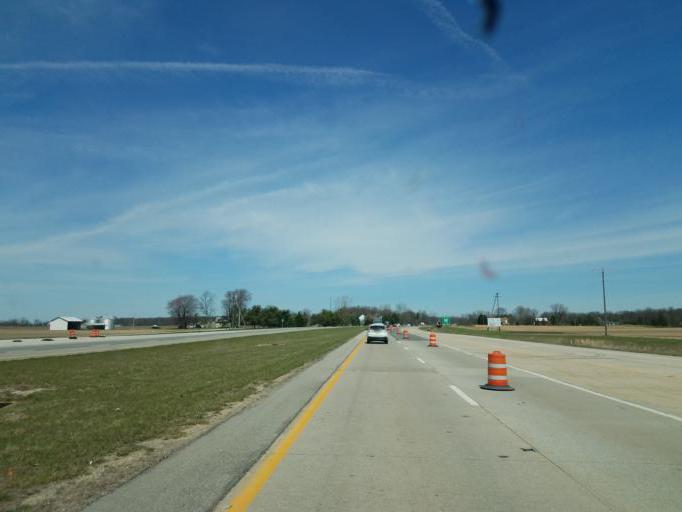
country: US
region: Ohio
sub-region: Marion County
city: Prospect
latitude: 40.4251
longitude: -83.0742
